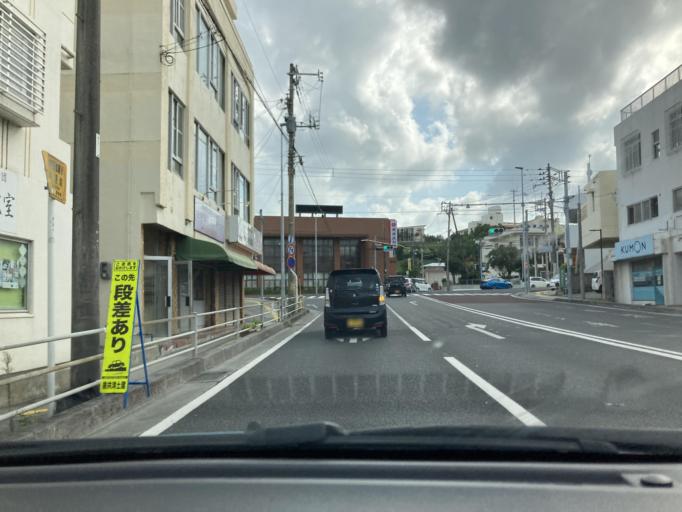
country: JP
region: Okinawa
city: Ginowan
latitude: 26.2022
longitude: 127.7545
